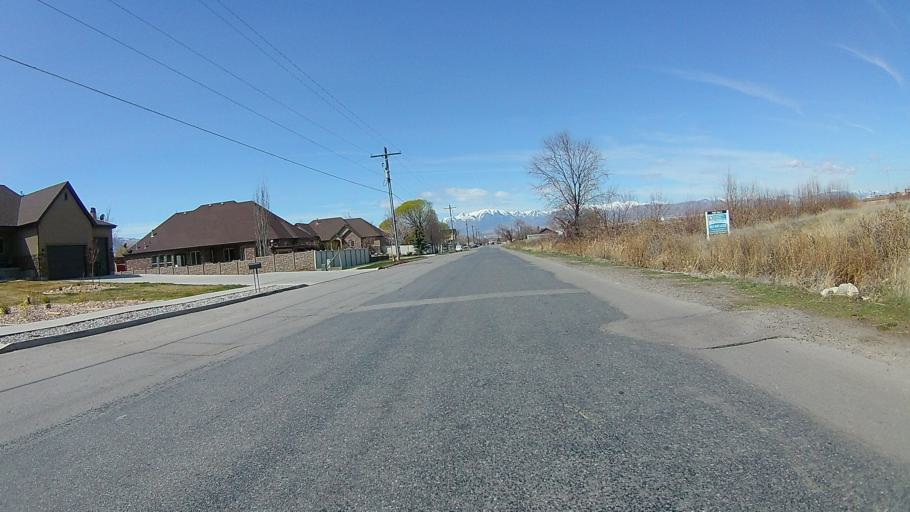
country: US
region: Utah
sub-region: Utah County
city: American Fork
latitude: 40.3727
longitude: -111.8148
